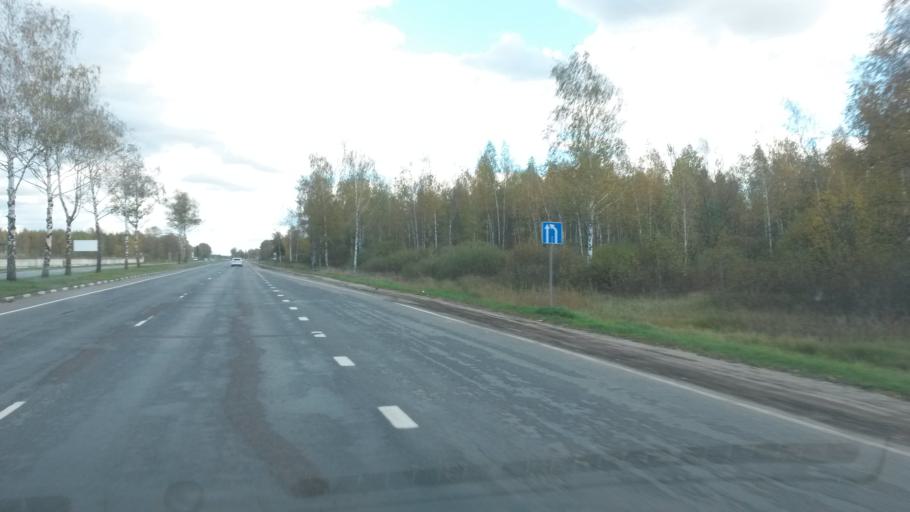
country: RU
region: Jaroslavl
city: Yaroslavl
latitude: 57.5407
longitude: 39.9808
